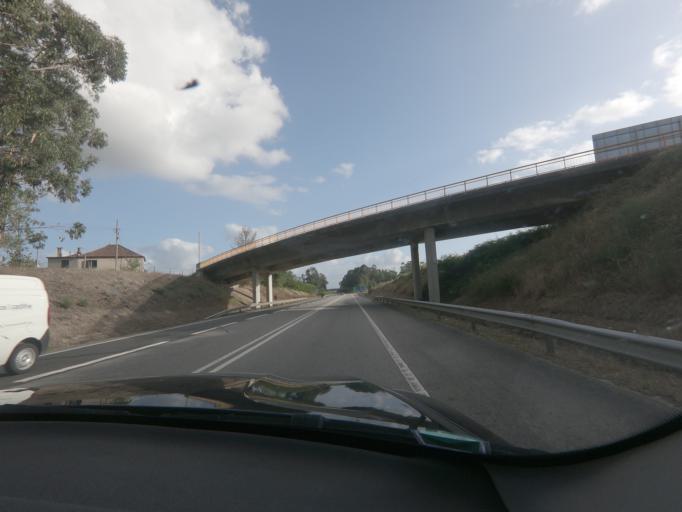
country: PT
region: Viseu
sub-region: Concelho de Tondela
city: Tondela
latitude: 40.5481
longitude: -8.0538
